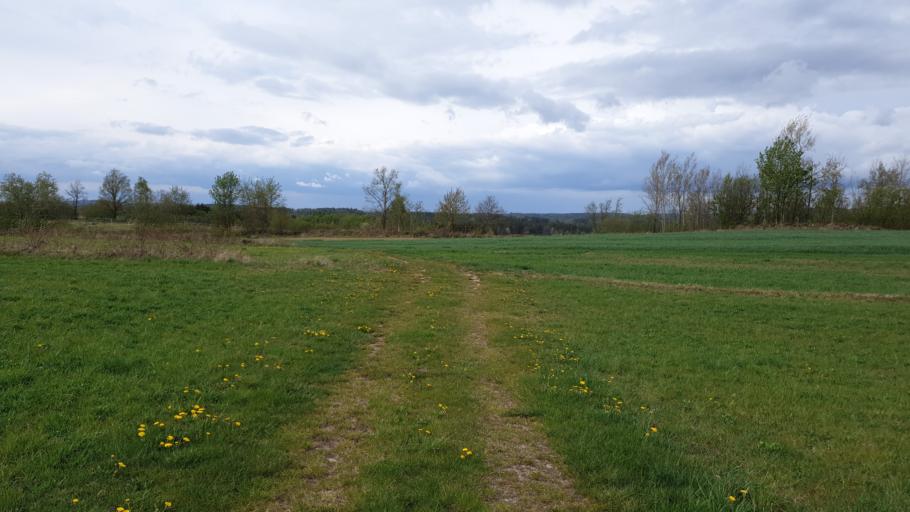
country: AT
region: Lower Austria
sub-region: Politischer Bezirk Gmund
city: Weitra
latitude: 48.6649
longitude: 14.9375
